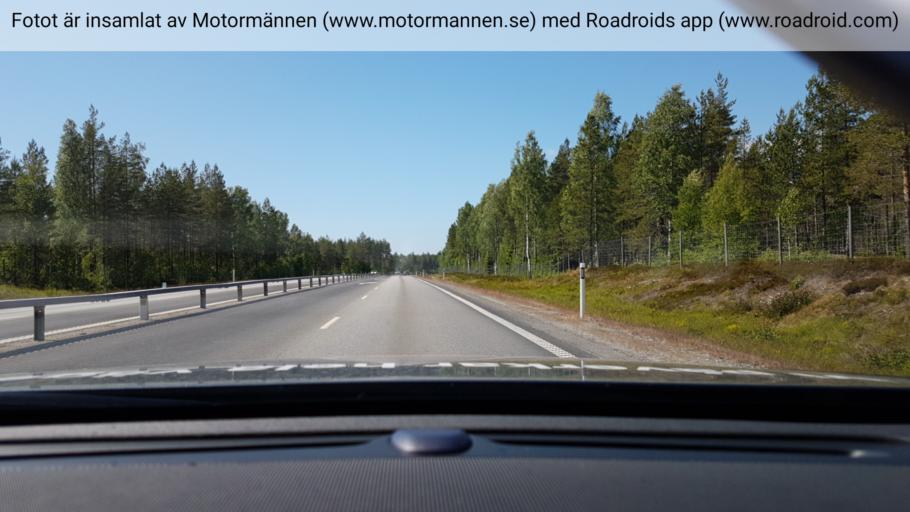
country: SE
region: Vaesterbotten
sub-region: Umea Kommun
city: Hoernefors
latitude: 63.6038
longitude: 19.7639
